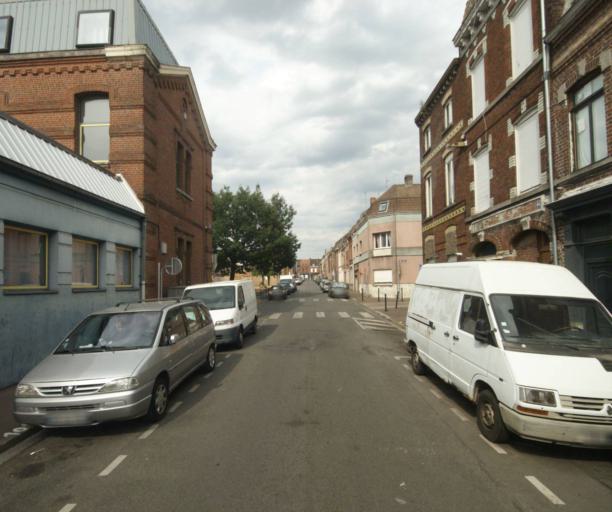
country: FR
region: Nord-Pas-de-Calais
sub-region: Departement du Nord
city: Roubaix
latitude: 50.6954
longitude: 3.1577
